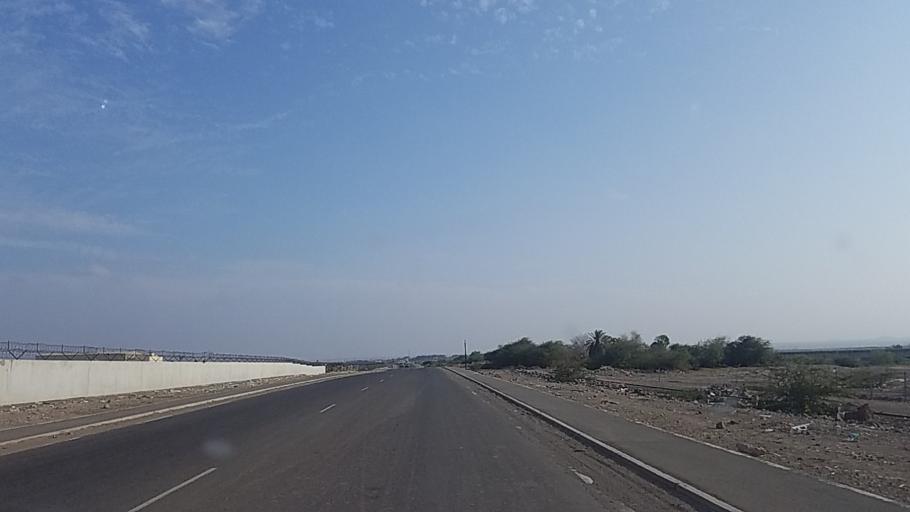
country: DJ
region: Djibouti
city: Djibouti
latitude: 11.5503
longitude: 43.1426
